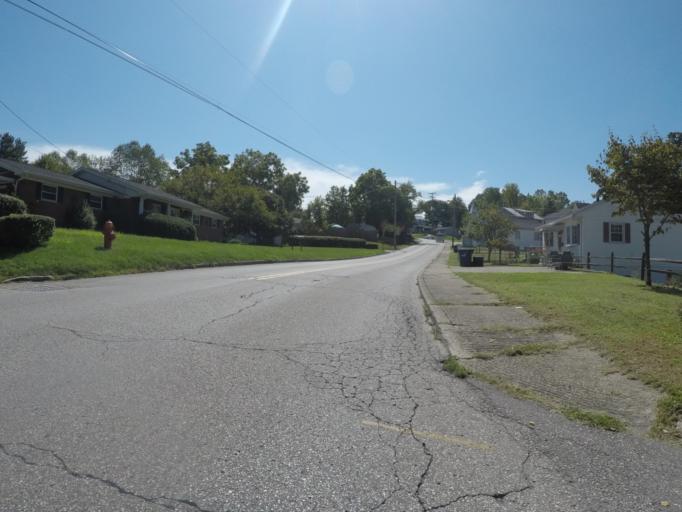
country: US
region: Kentucky
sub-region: Boyd County
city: Ashland
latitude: 38.4587
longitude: -82.6491
